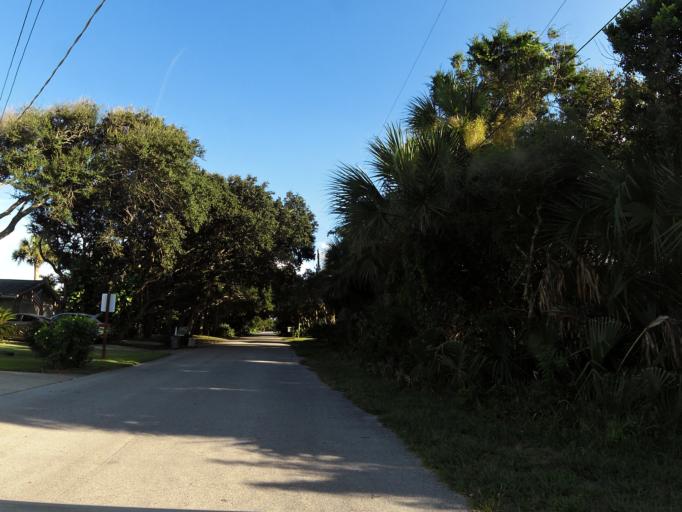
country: US
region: Florida
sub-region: Flagler County
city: Flagler Beach
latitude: 29.4589
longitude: -81.1205
